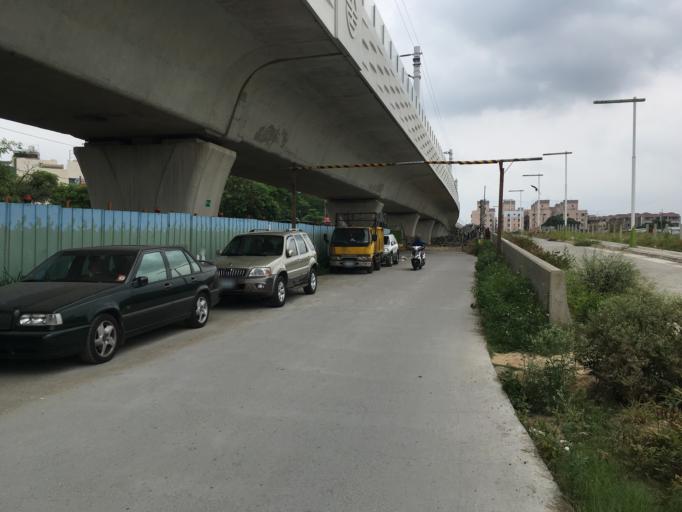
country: TW
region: Taiwan
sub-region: Taichung City
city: Taichung
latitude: 24.1840
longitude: 120.7026
